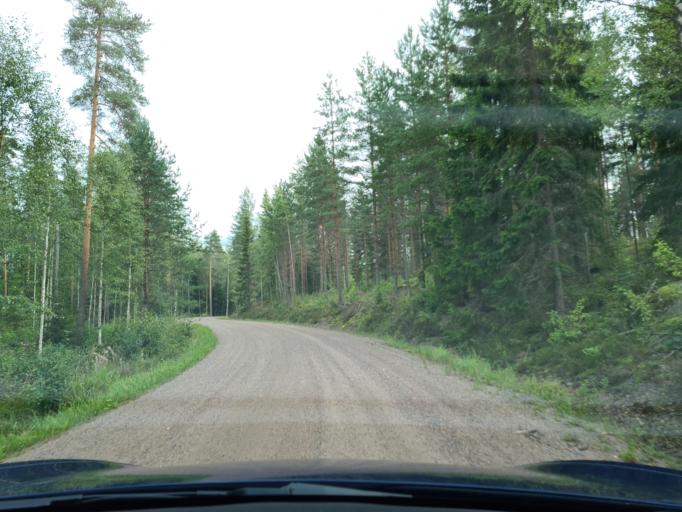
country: FI
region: Uusimaa
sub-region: Helsinki
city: Vihti
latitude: 60.4184
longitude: 24.4817
